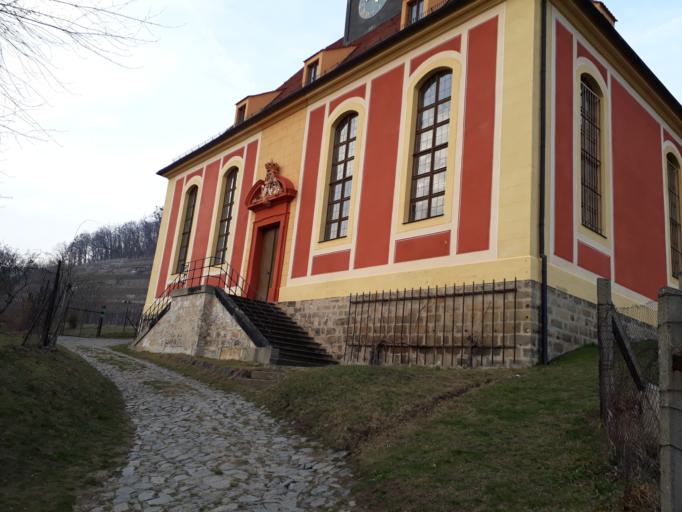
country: DE
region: Saxony
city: Heidenau
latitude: 51.0111
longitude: 13.8783
